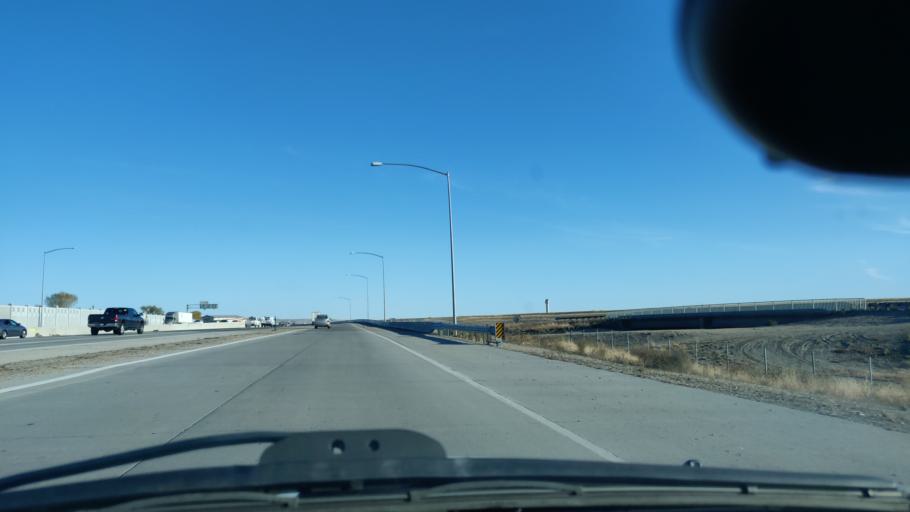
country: US
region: Idaho
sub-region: Ada County
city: Garden City
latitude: 43.5734
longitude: -116.2410
